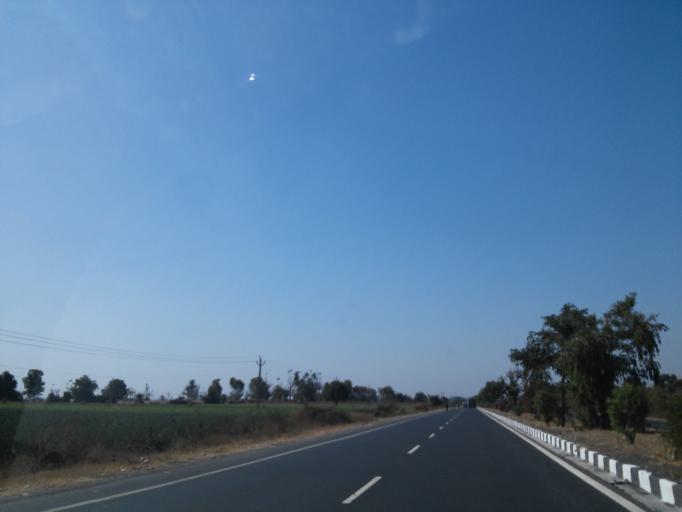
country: IN
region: Gujarat
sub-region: Sabar Kantha
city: Modasa
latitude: 23.6048
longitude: 73.2240
